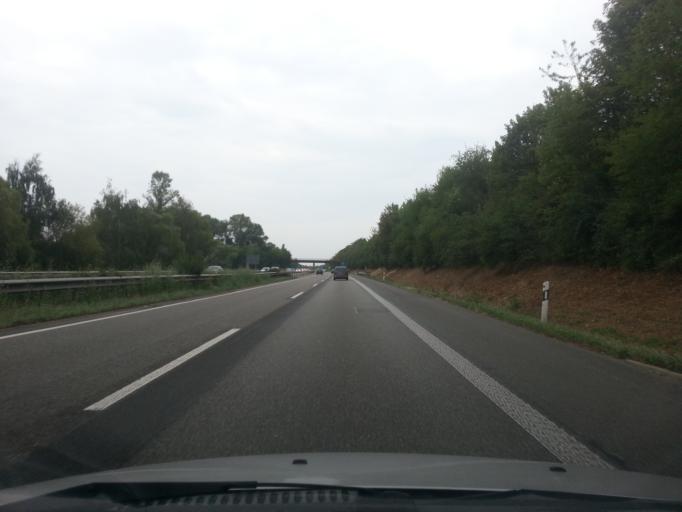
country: DE
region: Rheinland-Pfalz
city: Bornheim
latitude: 49.2060
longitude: 8.1478
